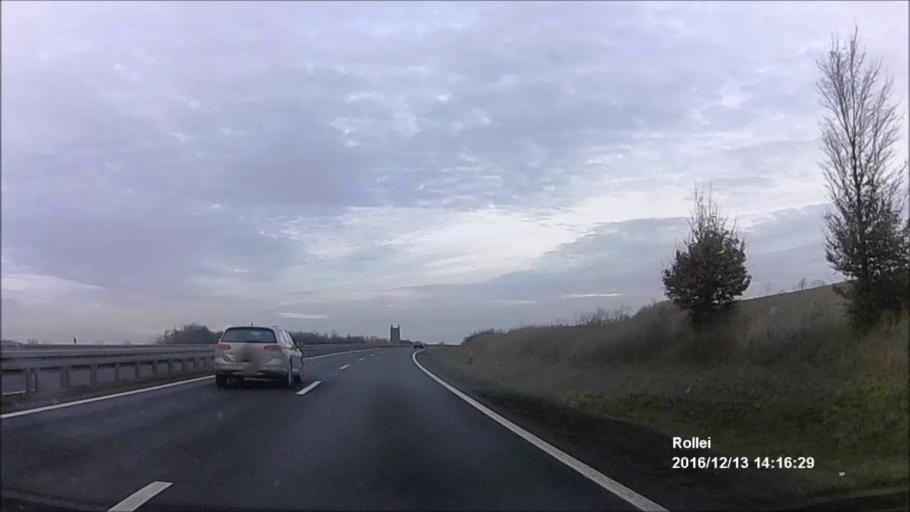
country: DE
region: Thuringia
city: Erfurt
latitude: 51.0176
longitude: 11.0579
